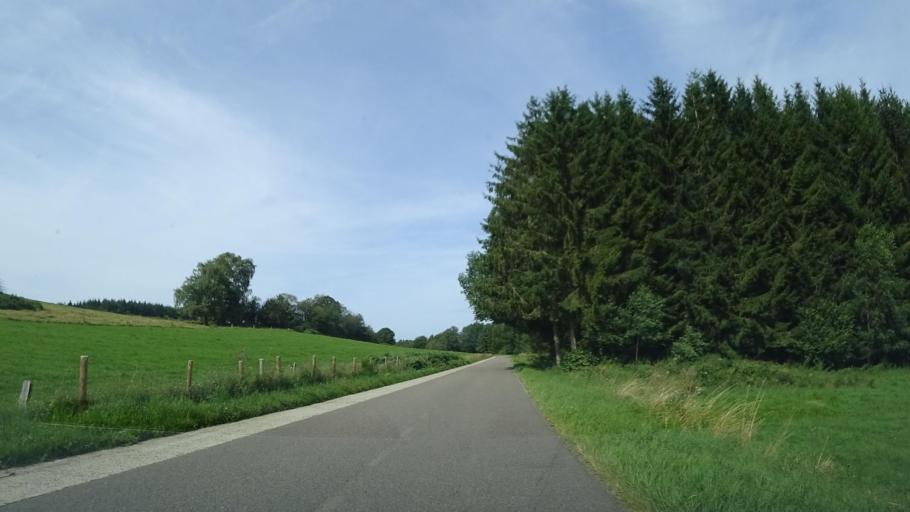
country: BE
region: Wallonia
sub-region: Province du Luxembourg
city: Bertrix
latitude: 49.8103
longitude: 5.3064
